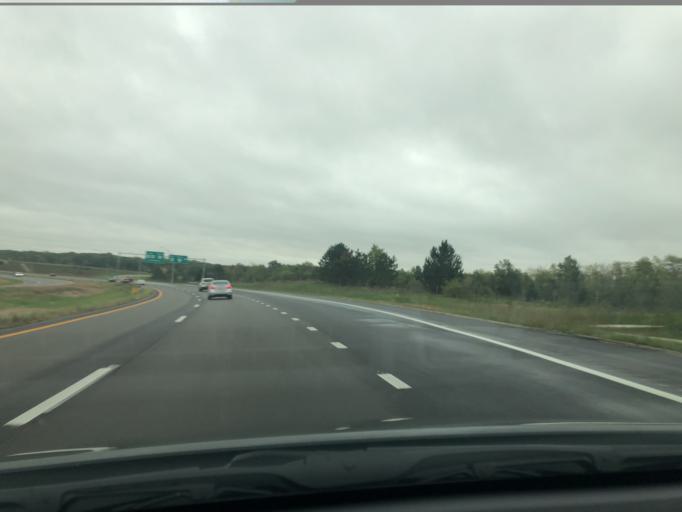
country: US
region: Ohio
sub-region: Union County
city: Marysville
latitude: 40.2367
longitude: -83.4063
